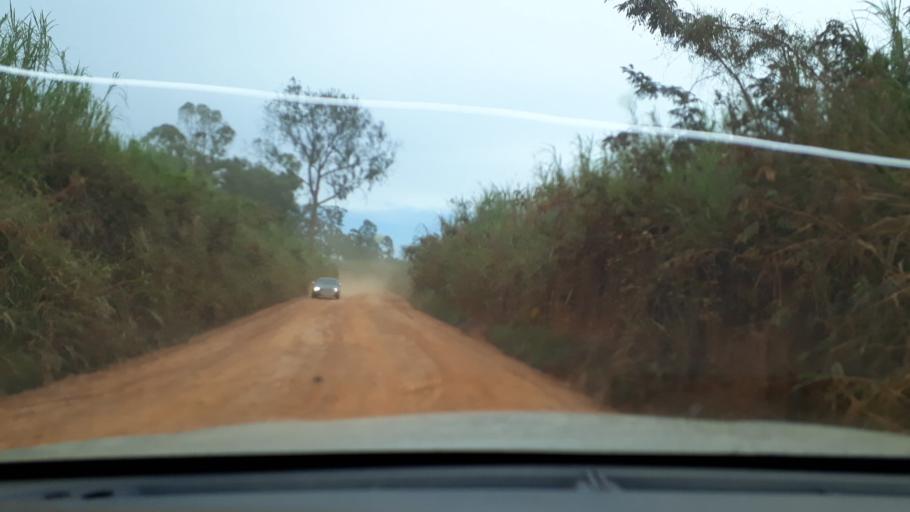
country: CD
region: Eastern Province
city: Bunia
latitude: 1.8421
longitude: 30.4639
